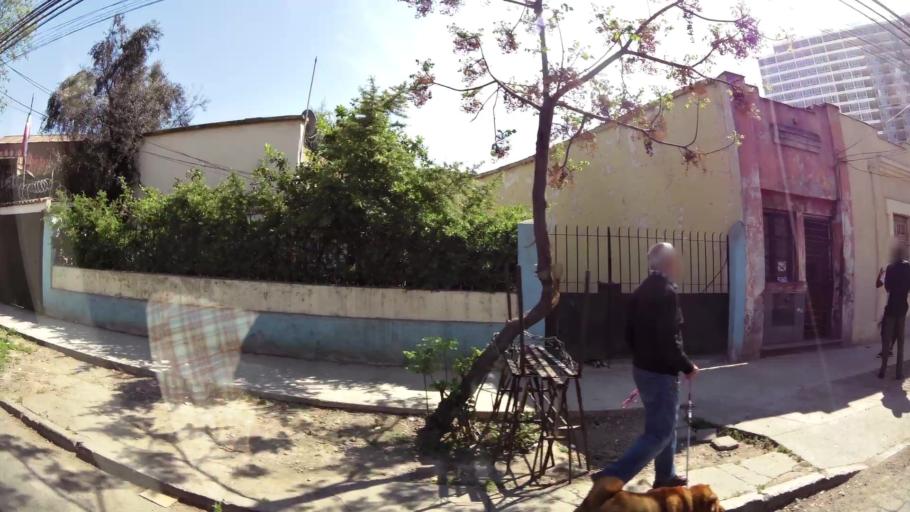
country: CL
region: Santiago Metropolitan
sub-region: Provincia de Santiago
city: Santiago
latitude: -33.4012
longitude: -70.6624
